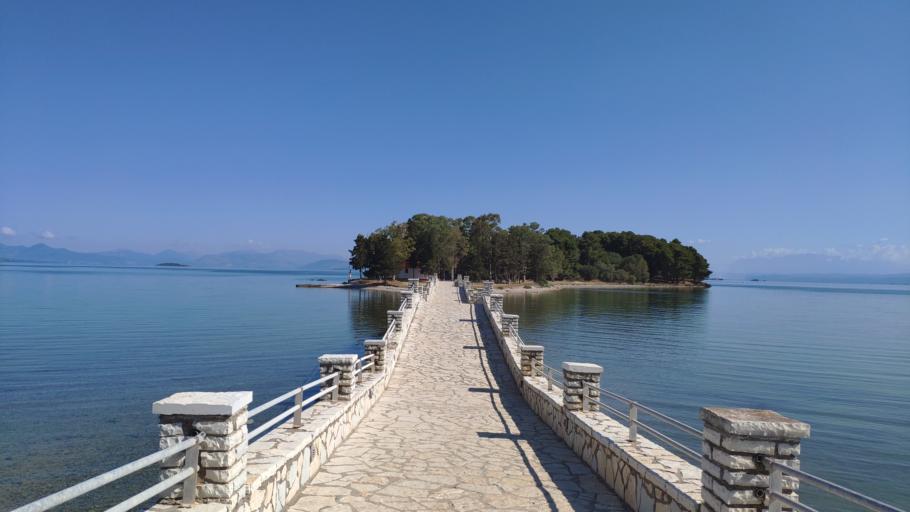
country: GR
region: West Greece
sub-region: Nomos Aitolias kai Akarnanias
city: Vonitsa
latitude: 38.9231
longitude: 20.9002
